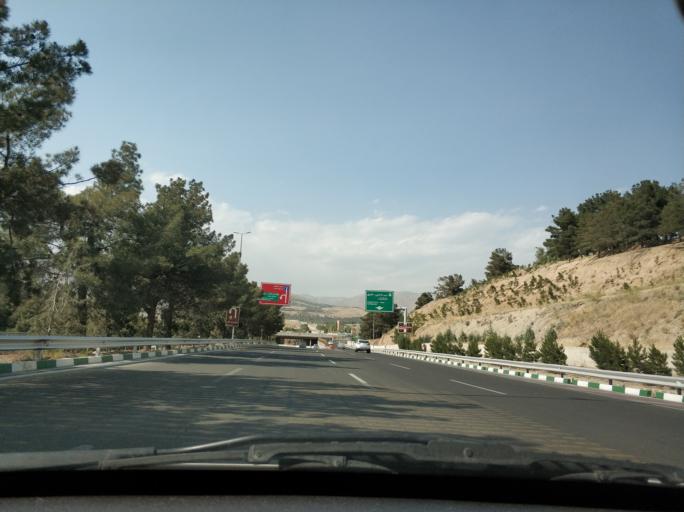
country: IR
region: Tehran
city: Tajrish
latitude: 35.7734
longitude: 51.5365
